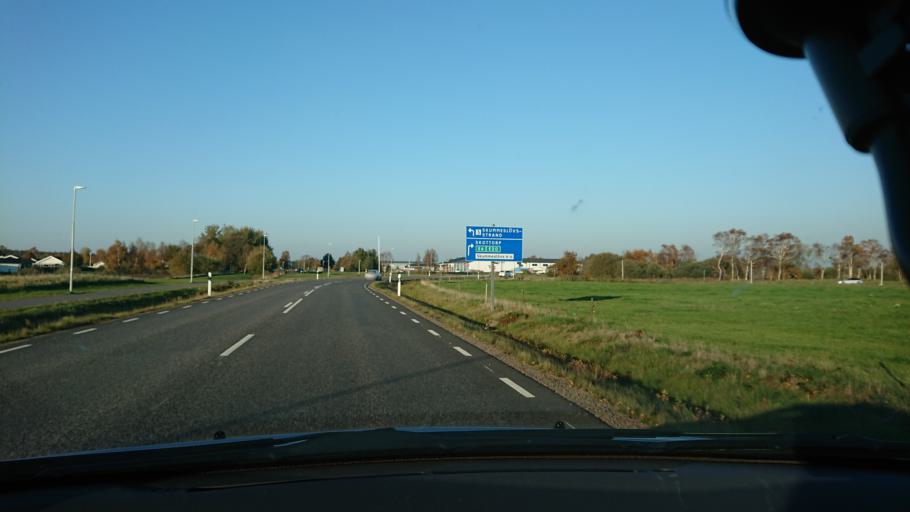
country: SE
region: Halland
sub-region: Laholms Kommun
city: Mellbystrand
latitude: 56.4529
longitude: 12.9358
